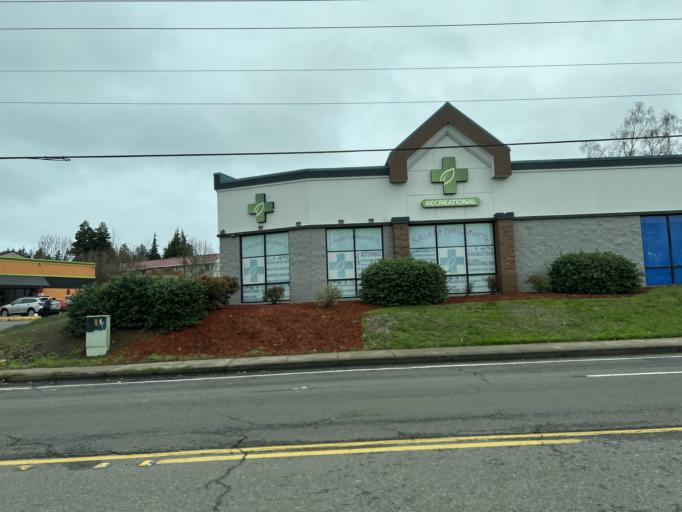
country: US
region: Oregon
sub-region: Marion County
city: Salem
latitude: 44.8840
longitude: -123.0315
